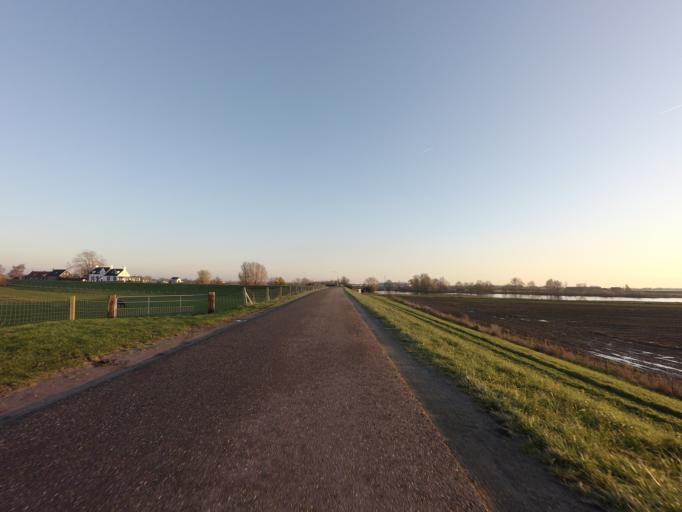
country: NL
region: Gelderland
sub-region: Gemeente Zaltbommel
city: Nederhemert-Noord
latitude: 51.7433
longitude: 5.2009
